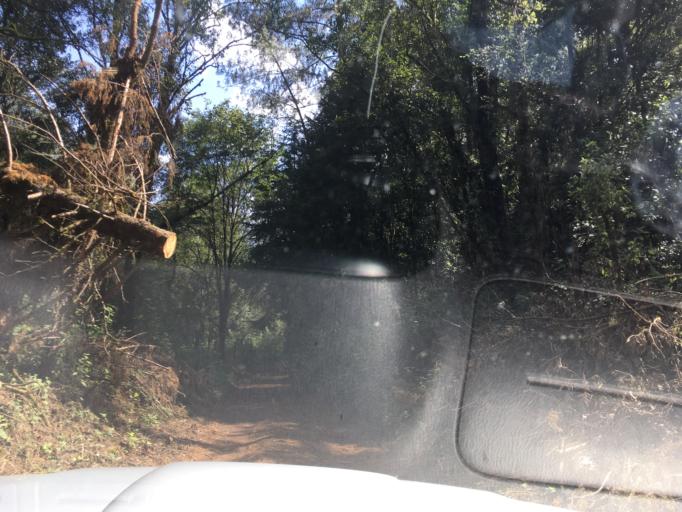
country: MX
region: Michoacan
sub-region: Zitacuaro
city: Francisco Serrato (San Bartolo)
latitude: 19.5049
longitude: -100.3062
